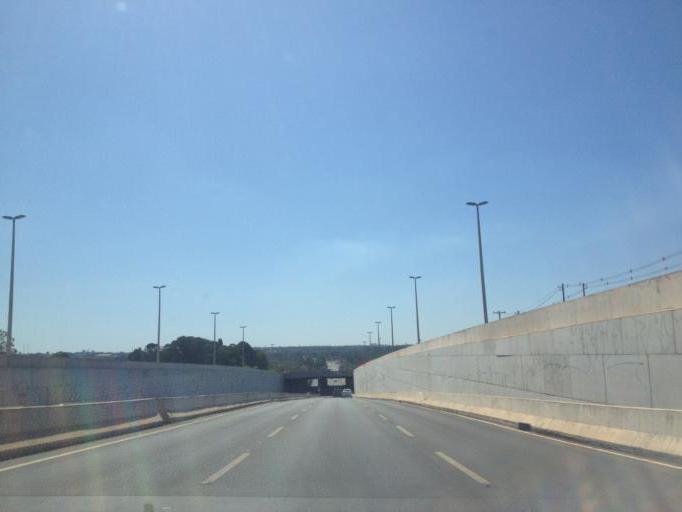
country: BR
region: Federal District
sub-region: Brasilia
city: Brasilia
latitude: -15.8644
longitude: -47.9358
